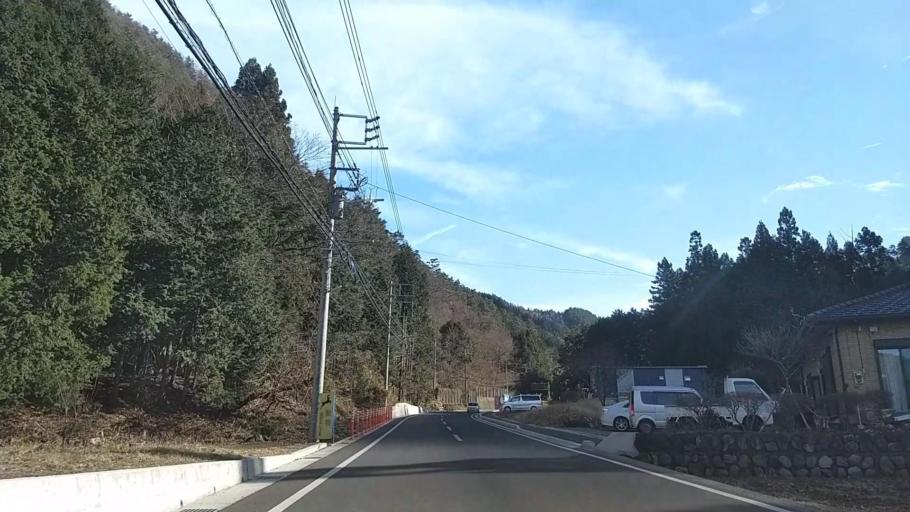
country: JP
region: Yamanashi
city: Otsuki
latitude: 35.5272
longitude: 138.9220
